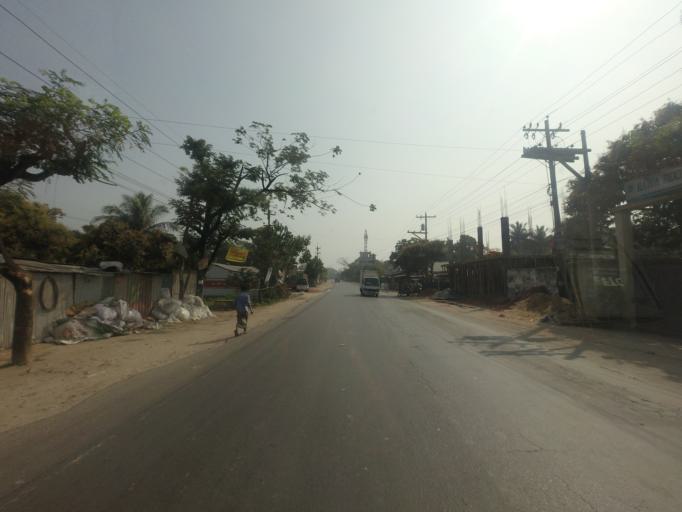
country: BD
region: Dhaka
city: Narsingdi
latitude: 23.8937
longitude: 90.6688
